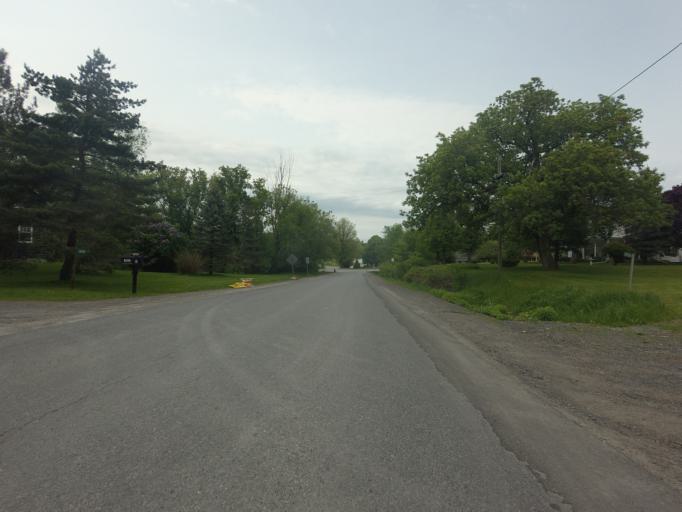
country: CA
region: Ontario
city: Kingston
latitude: 44.2980
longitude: -76.5601
